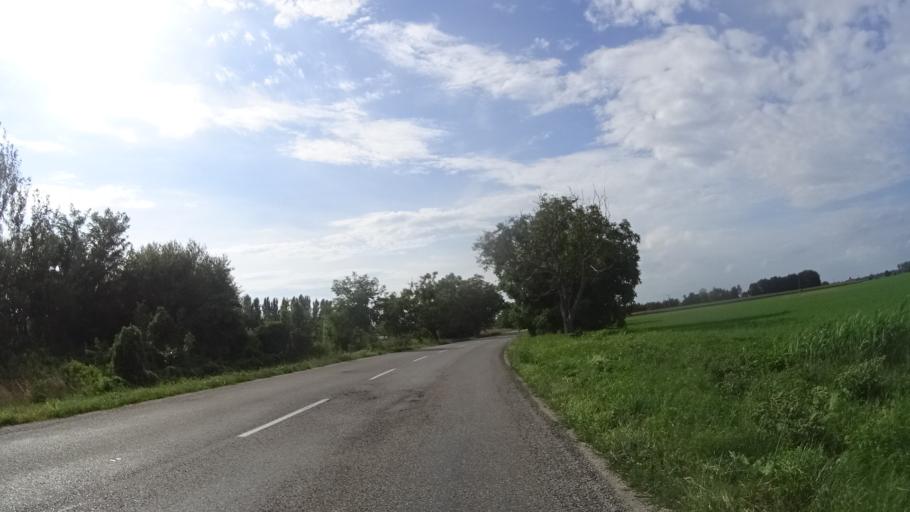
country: SK
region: Trnavsky
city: Gabcikovo
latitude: 47.9153
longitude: 17.5074
